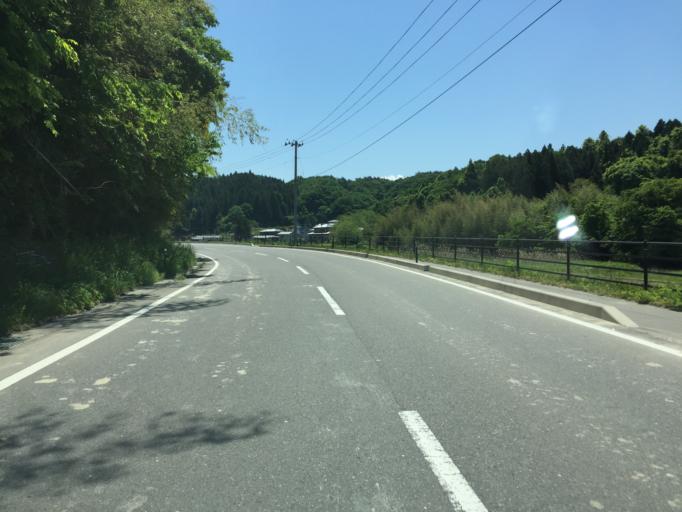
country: JP
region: Fukushima
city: Miharu
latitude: 37.5013
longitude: 140.4759
